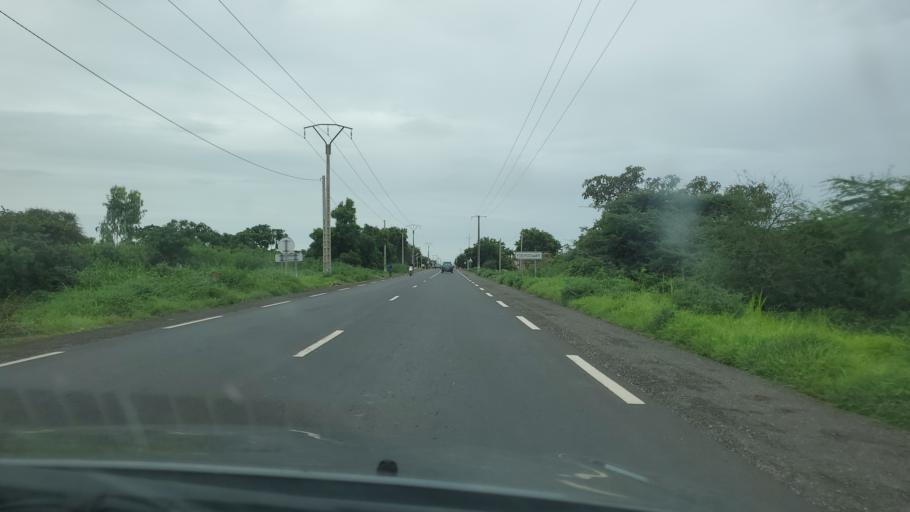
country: SN
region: Thies
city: Kayar
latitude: 15.0605
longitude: -16.9403
